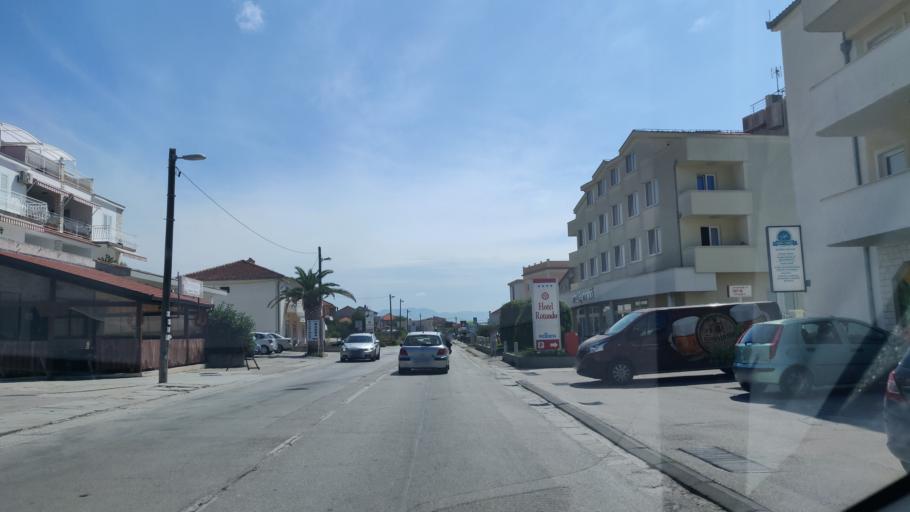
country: HR
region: Splitsko-Dalmatinska
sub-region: Grad Trogir
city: Trogir
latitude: 43.5189
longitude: 16.2324
